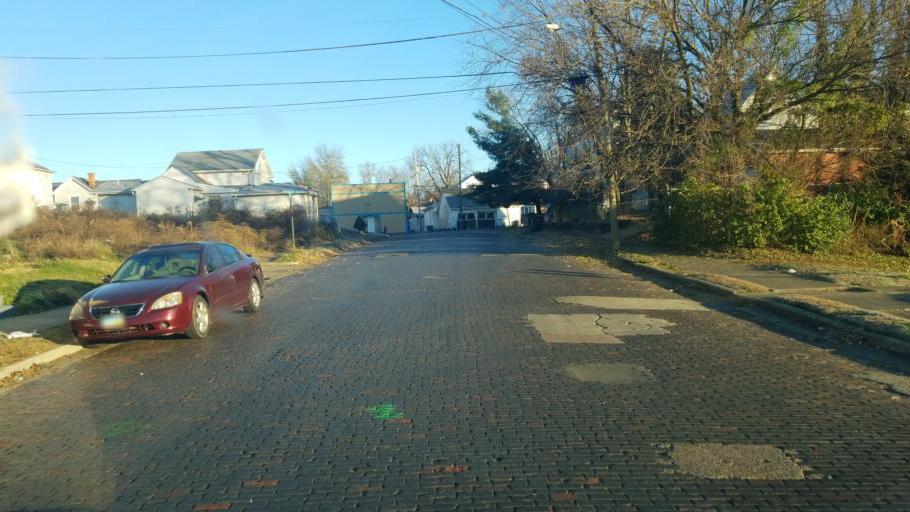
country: US
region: Kentucky
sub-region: Greenup County
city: South Shore
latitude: 38.7399
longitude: -82.9712
